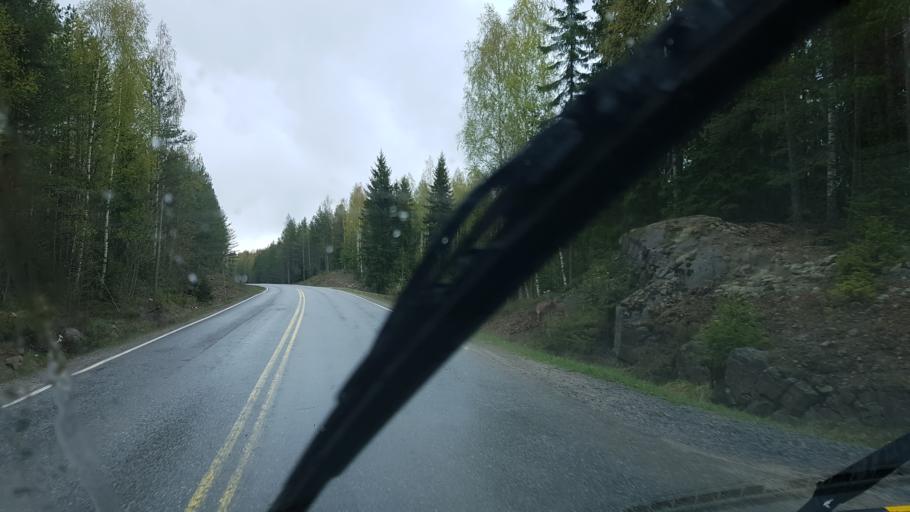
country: FI
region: Pirkanmaa
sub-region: Tampere
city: Pirkkala
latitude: 61.3963
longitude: 23.6267
